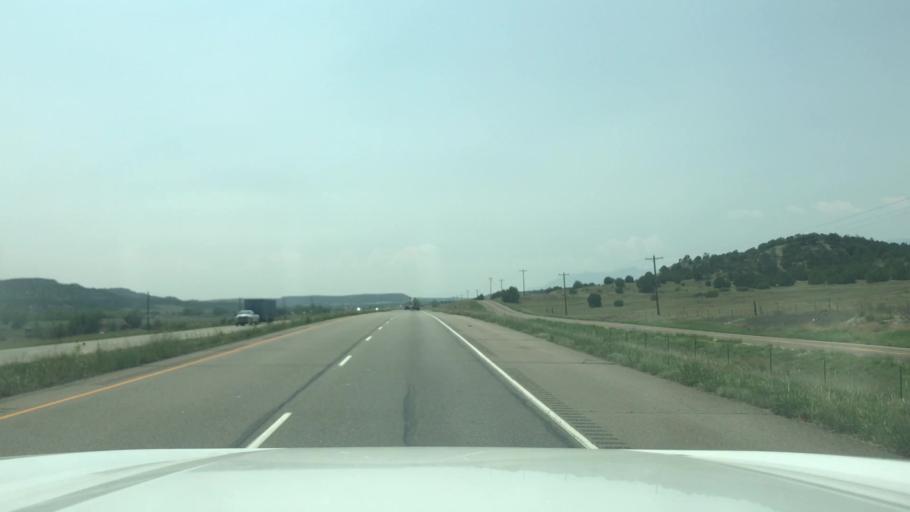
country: US
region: Colorado
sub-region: Pueblo County
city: Colorado City
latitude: 38.0188
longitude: -104.7404
